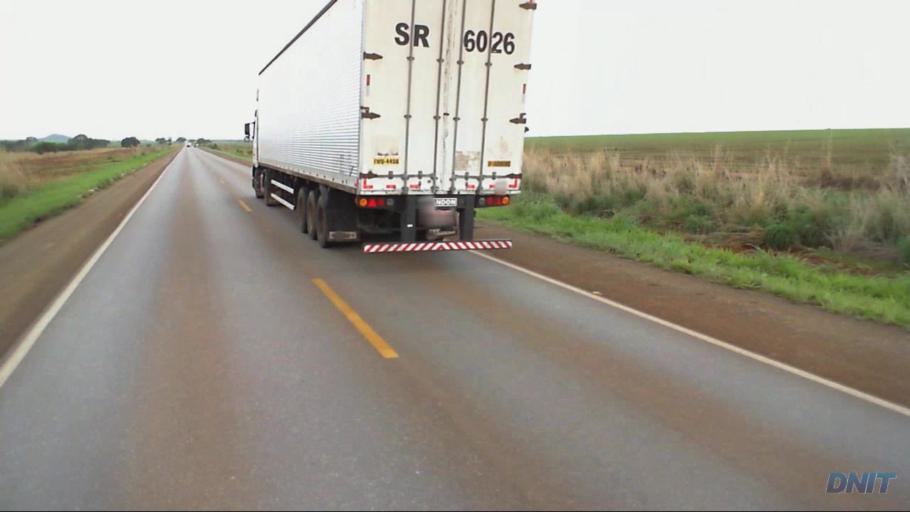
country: BR
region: Goias
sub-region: Barro Alto
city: Barro Alto
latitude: -14.8279
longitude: -49.0360
